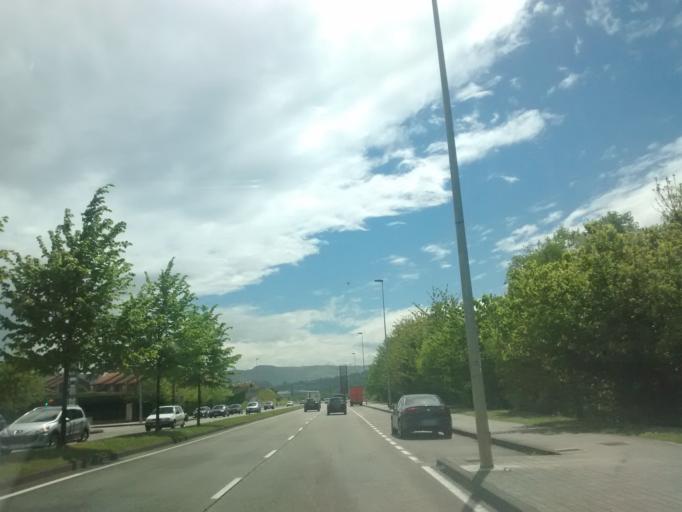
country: ES
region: Asturias
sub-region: Province of Asturias
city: Gijon
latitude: 43.5317
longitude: -5.6345
